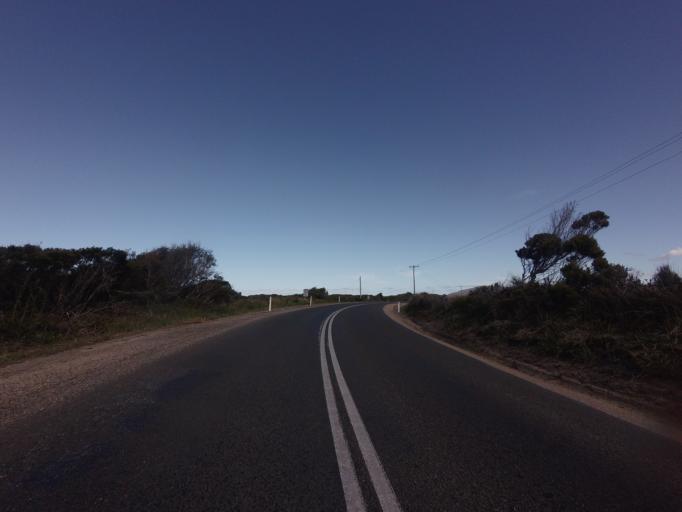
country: AU
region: Tasmania
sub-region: Break O'Day
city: St Helens
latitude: -41.8029
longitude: 148.2625
